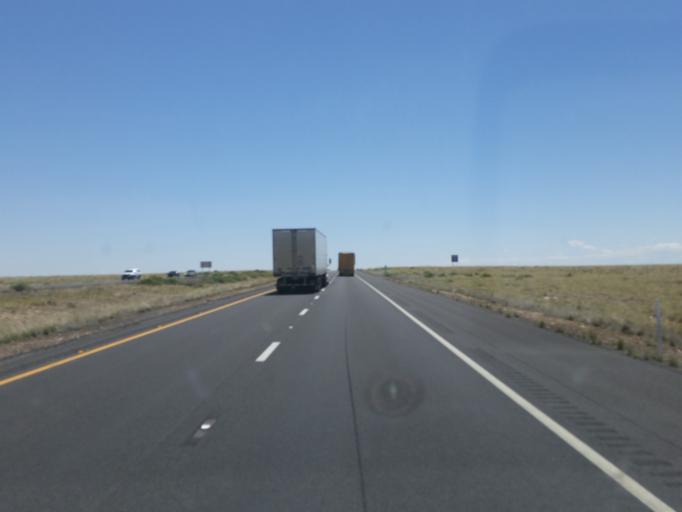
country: US
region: Arizona
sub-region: Coconino County
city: Flagstaff
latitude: 35.1358
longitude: -111.2024
